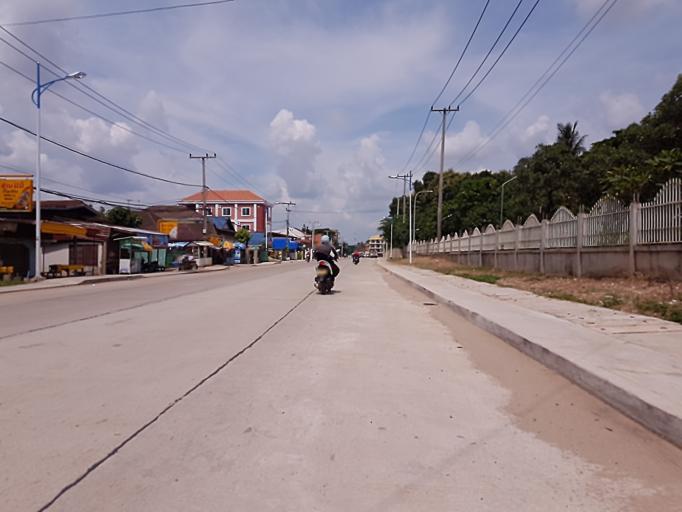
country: TH
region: Nong Khai
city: Si Chiang Mai
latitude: 17.9068
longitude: 102.6187
